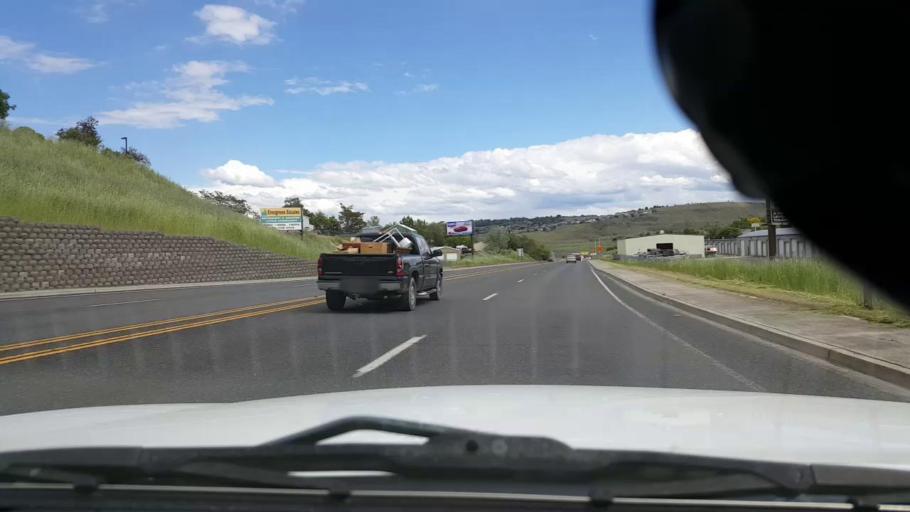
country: US
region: Washington
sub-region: Asotin County
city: West Clarkston-Highland
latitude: 46.4013
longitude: -117.0552
